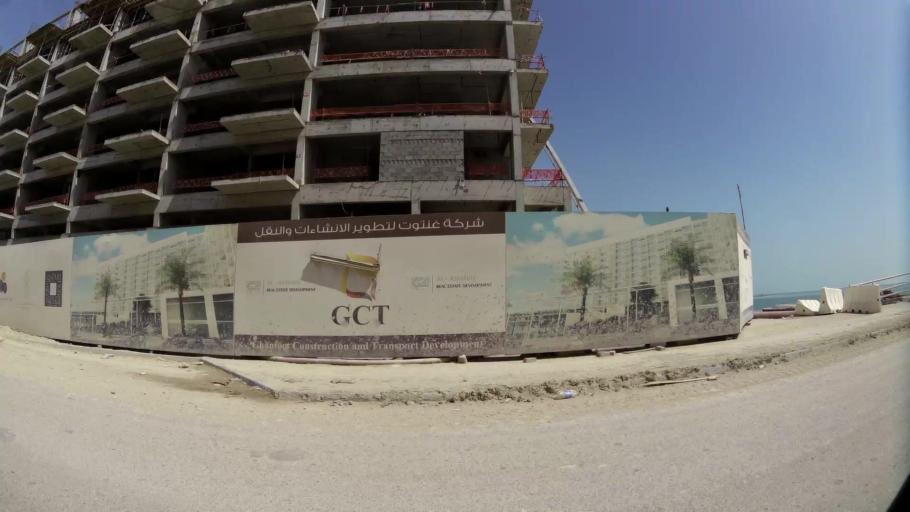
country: QA
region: Baladiyat Umm Salal
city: Umm Salal Muhammad
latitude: 25.4049
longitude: 51.5231
